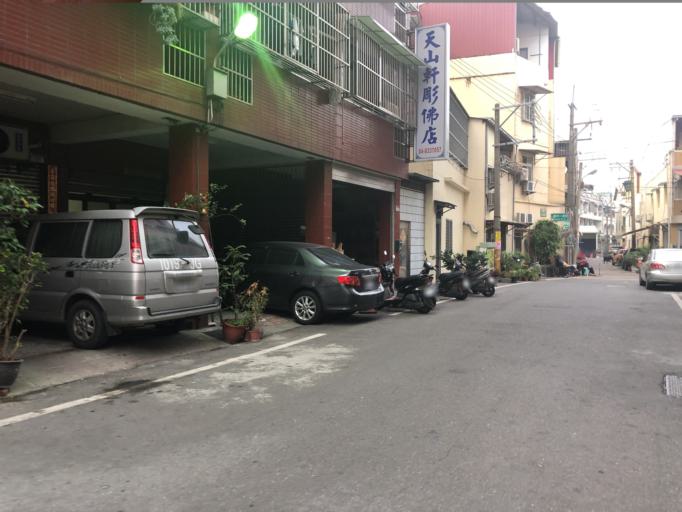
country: TW
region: Taiwan
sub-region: Changhua
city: Chang-hua
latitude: 23.9646
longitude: 120.5637
